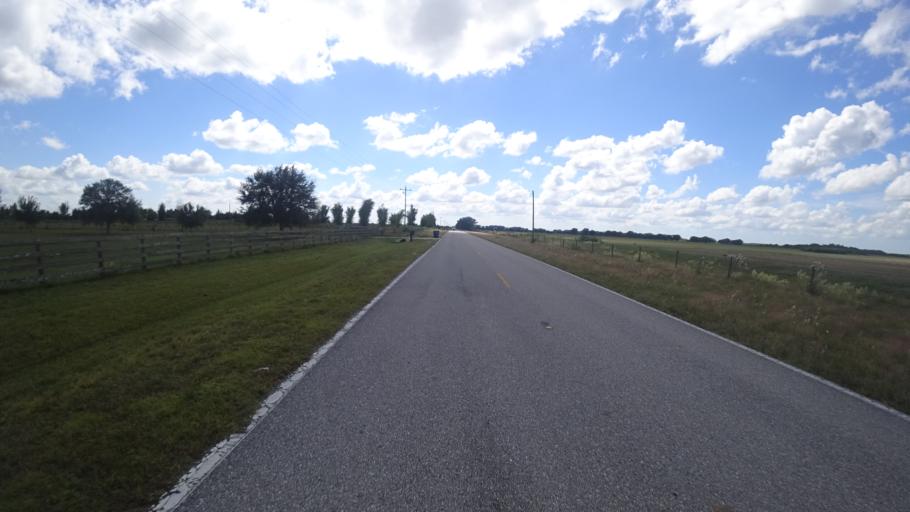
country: US
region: Florida
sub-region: Sarasota County
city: Warm Mineral Springs
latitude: 27.2970
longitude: -82.1894
